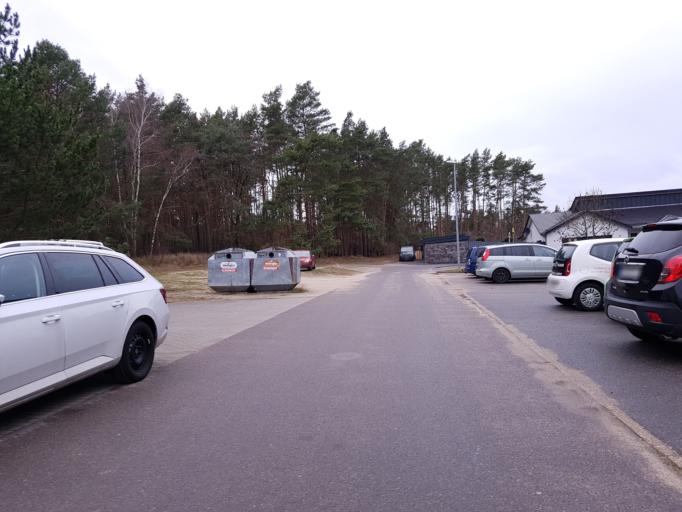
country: DE
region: Brandenburg
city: Groden
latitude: 51.4012
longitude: 13.5633
